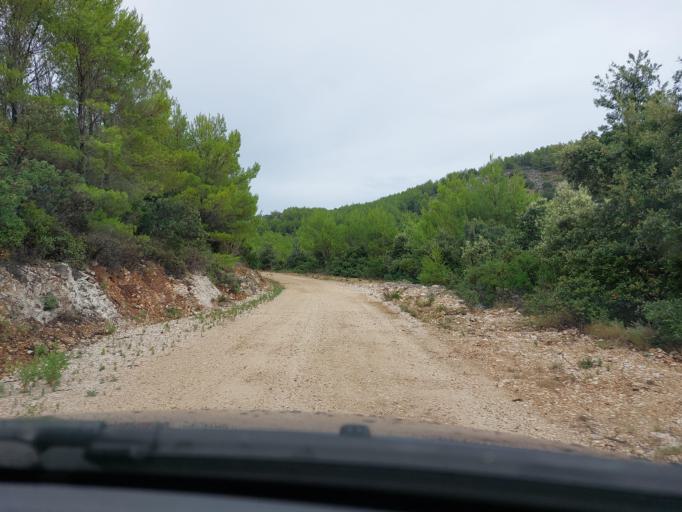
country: HR
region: Dubrovacko-Neretvanska
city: Smokvica
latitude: 42.7453
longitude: 16.9160
